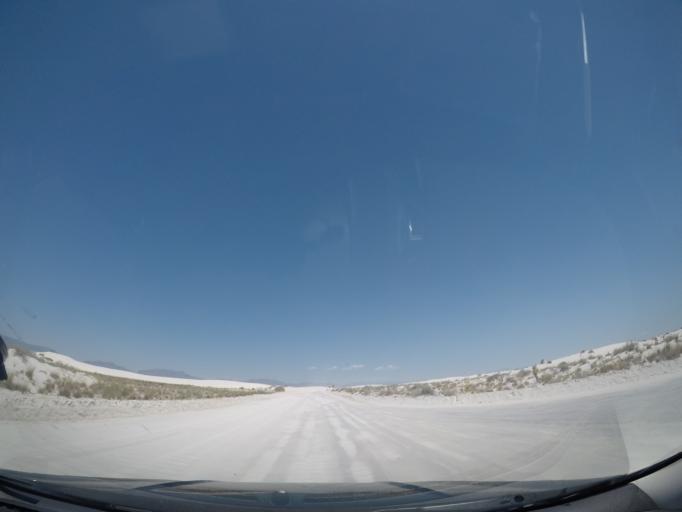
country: US
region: New Mexico
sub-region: Otero County
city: Holloman Air Force Base
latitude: 32.7963
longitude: -106.2465
